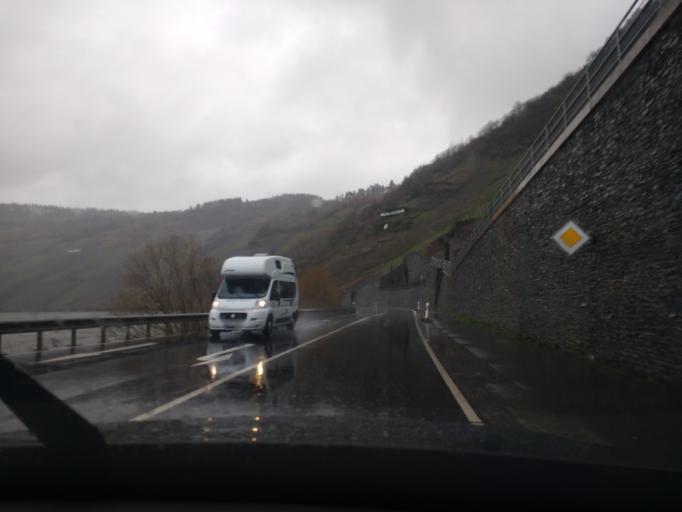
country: DE
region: Rheinland-Pfalz
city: Enkirch
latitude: 49.9785
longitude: 7.1084
